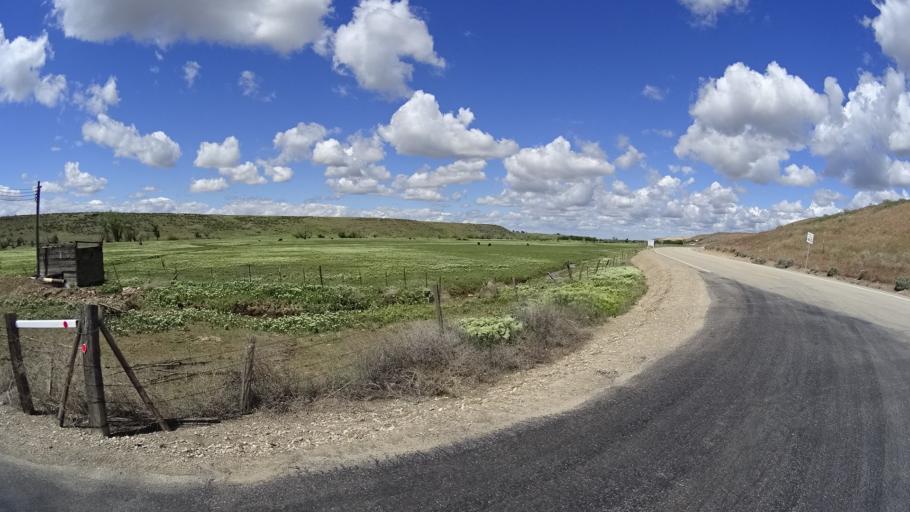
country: US
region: Idaho
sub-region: Ada County
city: Garden City
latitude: 43.4933
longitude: -116.2743
